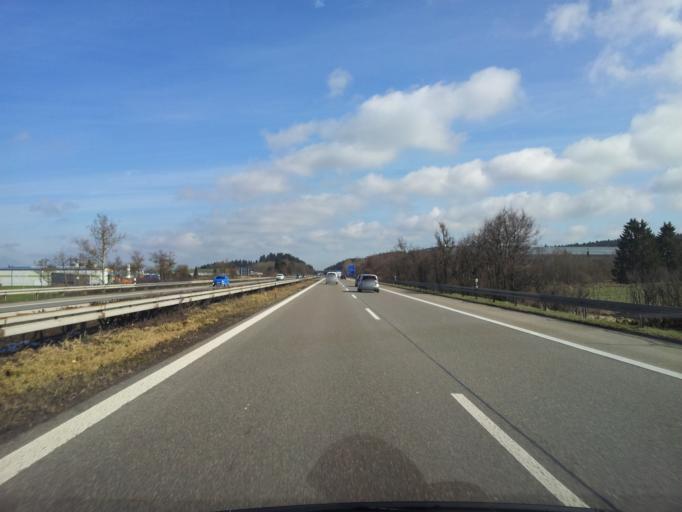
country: DE
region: Baden-Wuerttemberg
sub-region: Freiburg Region
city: Tuningen
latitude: 48.0248
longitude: 8.6133
